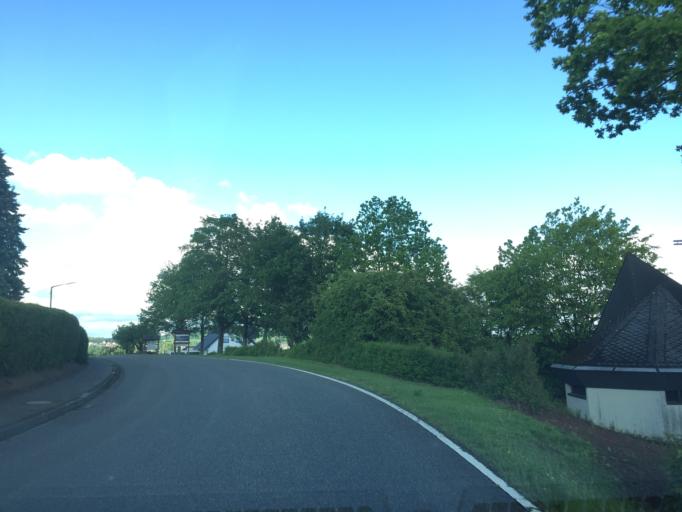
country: DE
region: Rheinland-Pfalz
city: Meudt
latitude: 50.4956
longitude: 7.8995
